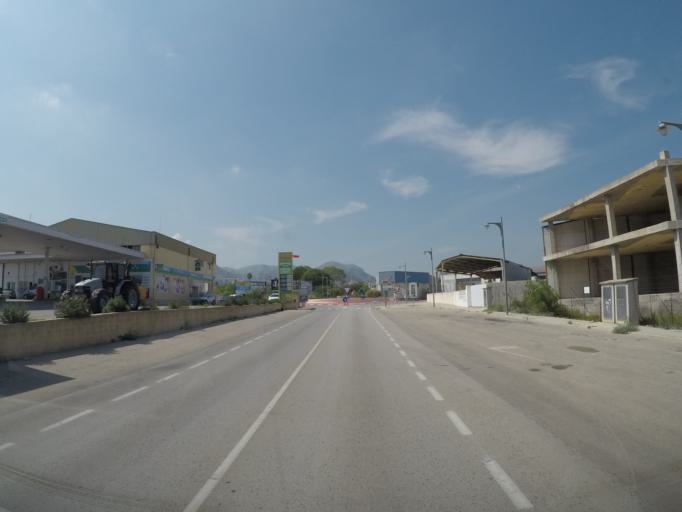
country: ES
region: Valencia
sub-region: Provincia de Alicante
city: Pego
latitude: 38.8440
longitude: -0.1066
